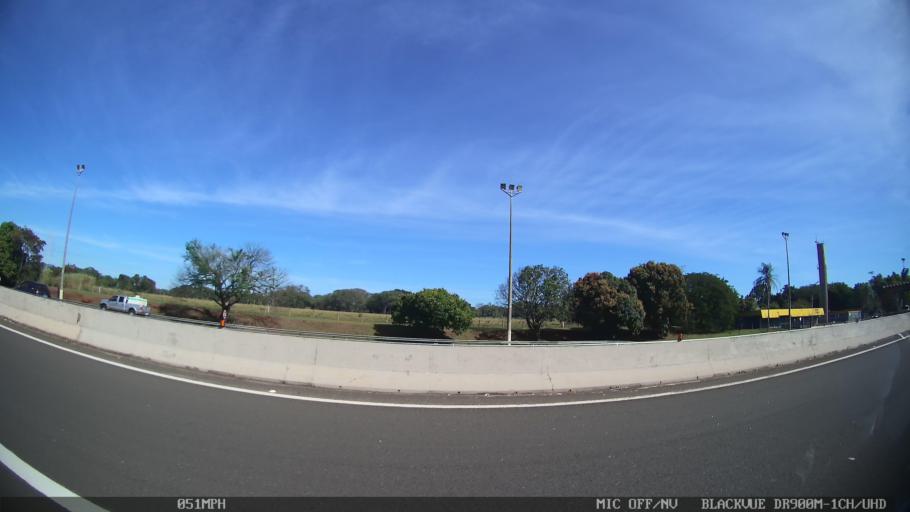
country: BR
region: Sao Paulo
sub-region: Pirassununga
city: Pirassununga
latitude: -21.9590
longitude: -47.4591
